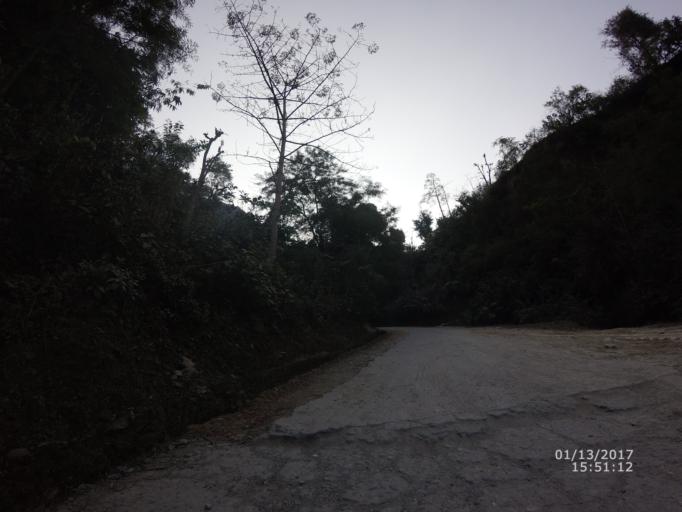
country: NP
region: Western Region
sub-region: Gandaki Zone
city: Pokhara
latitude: 28.1582
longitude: 84.0116
